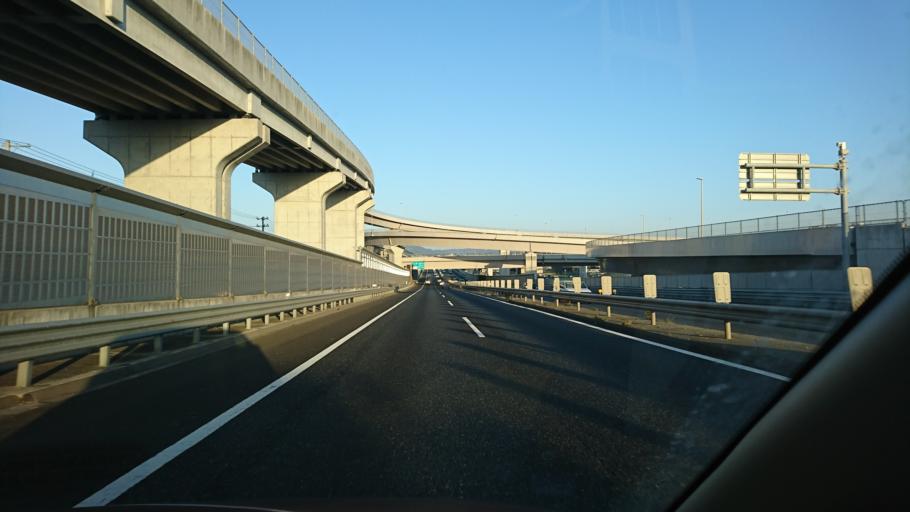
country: JP
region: Hyogo
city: Kakogawacho-honmachi
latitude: 34.7608
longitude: 134.8558
